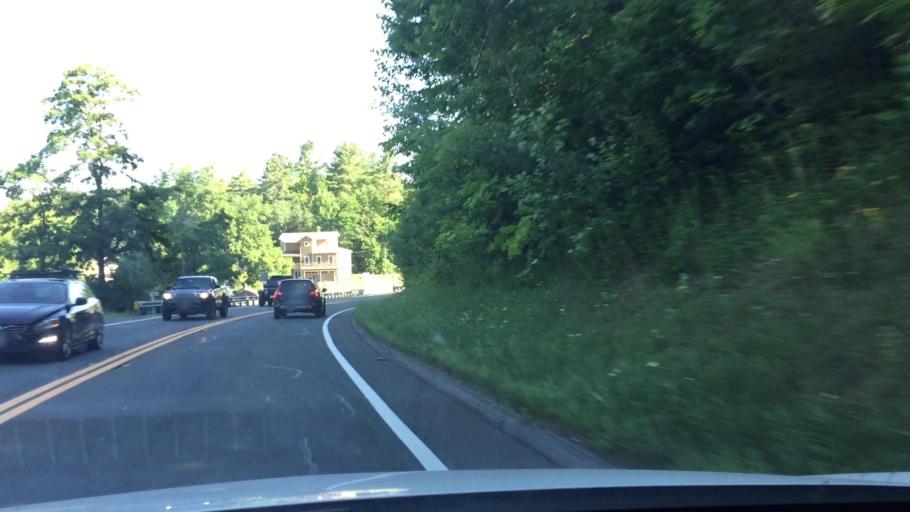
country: US
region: Massachusetts
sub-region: Berkshire County
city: Lee
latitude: 42.3234
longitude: -73.2606
